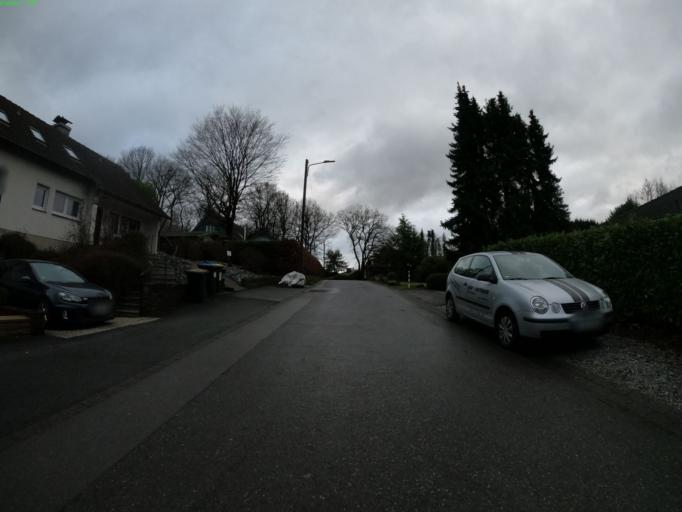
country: DE
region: North Rhine-Westphalia
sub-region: Regierungsbezirk Dusseldorf
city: Remscheid
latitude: 51.1822
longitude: 7.1398
